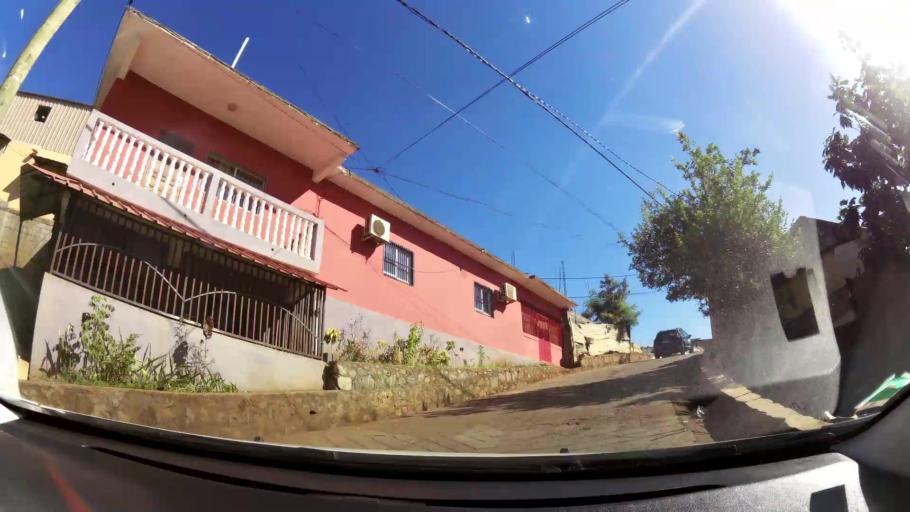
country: YT
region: Mamoudzou
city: Mamoudzou
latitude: -12.7895
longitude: 45.2189
